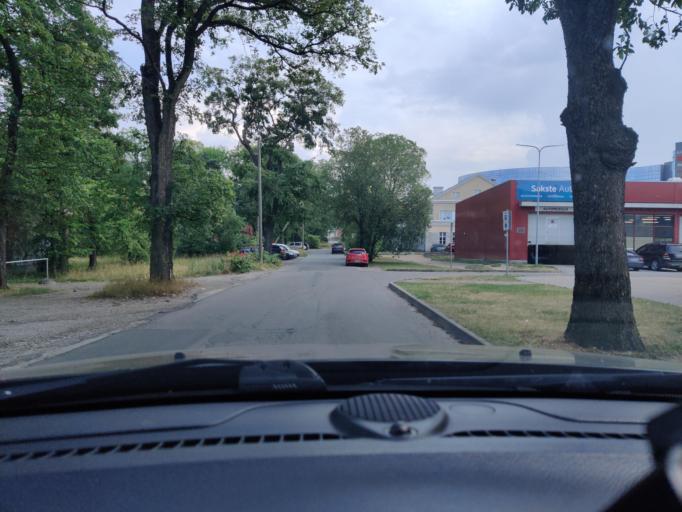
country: EE
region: Harju
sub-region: Tallinna linn
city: Tallinn
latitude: 59.4037
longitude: 24.7160
